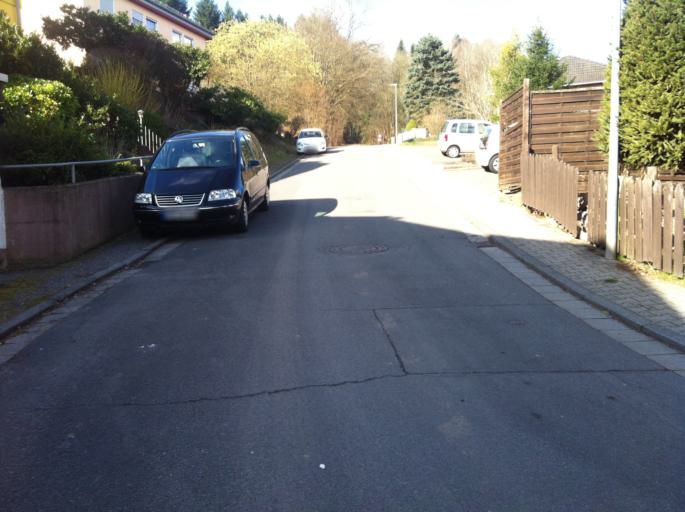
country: DE
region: Hesse
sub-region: Regierungsbezirk Darmstadt
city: Erbach
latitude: 49.6543
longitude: 8.9814
